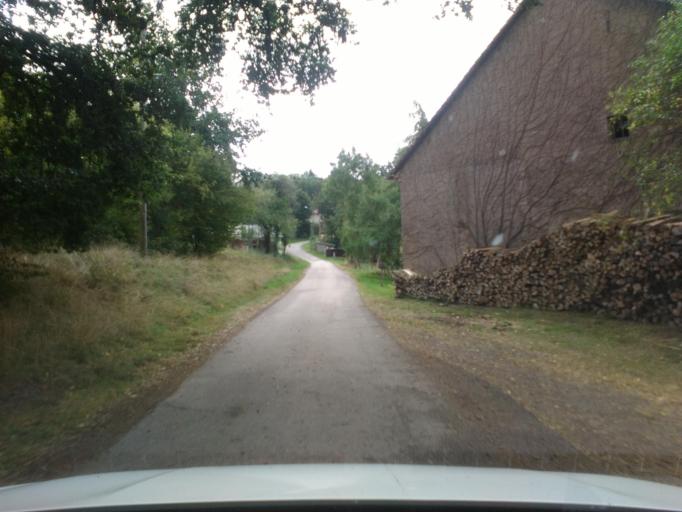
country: FR
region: Lorraine
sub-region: Departement des Vosges
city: Senones
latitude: 48.3576
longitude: 7.0090
